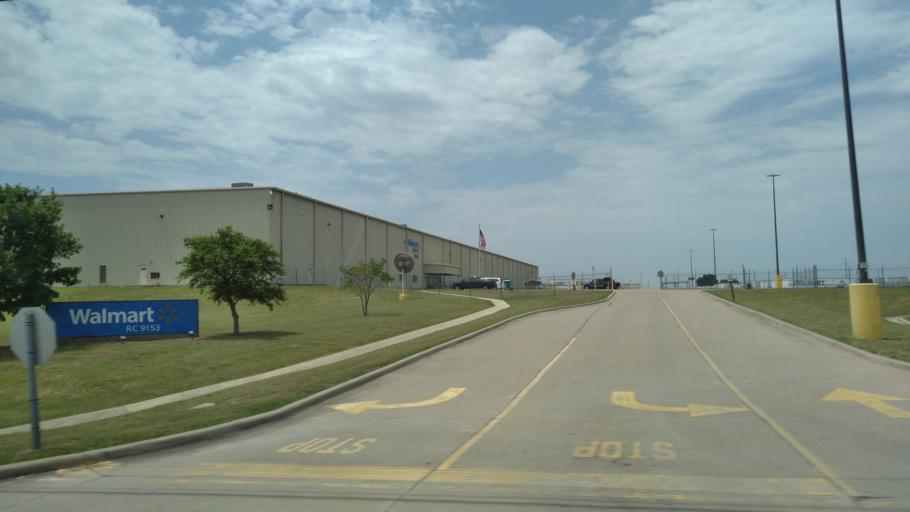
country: US
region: Texas
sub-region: McLennan County
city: Beverly Hills
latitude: 31.4926
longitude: -97.1649
